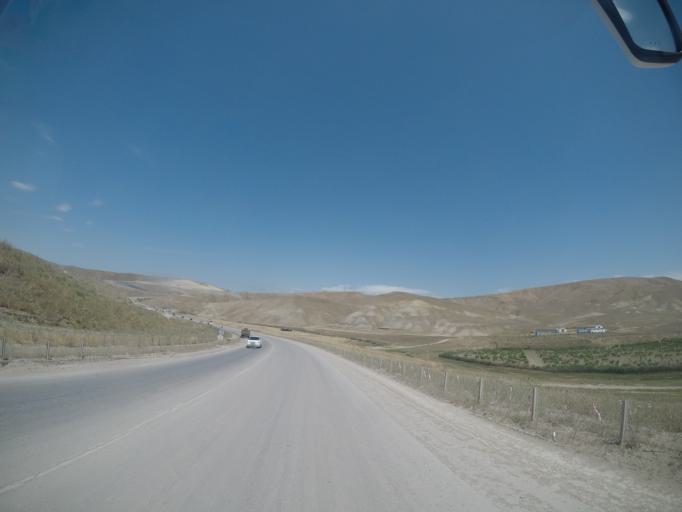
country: AZ
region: Samaxi
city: Shamakhi
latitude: 40.5542
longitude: 48.7641
